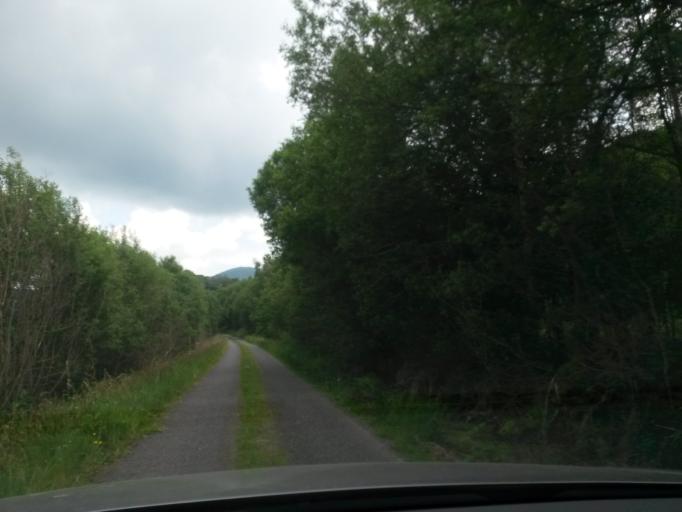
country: IE
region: Munster
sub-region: Ciarrai
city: Kenmare
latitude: 51.8368
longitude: -9.5200
